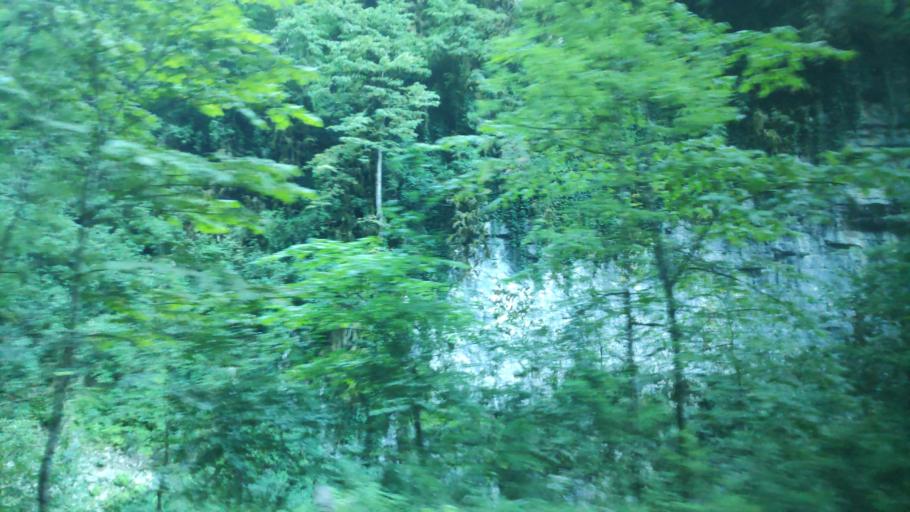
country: GE
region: Abkhazia
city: Gagra
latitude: 43.4369
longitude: 40.5329
